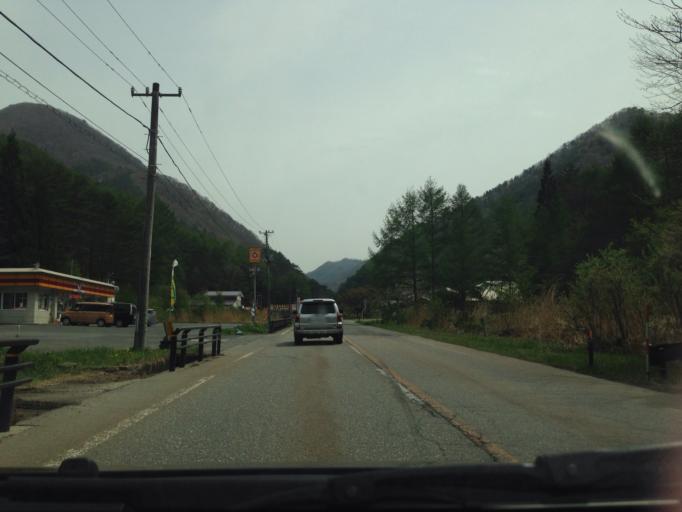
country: JP
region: Tochigi
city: Kuroiso
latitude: 37.1048
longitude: 139.7240
